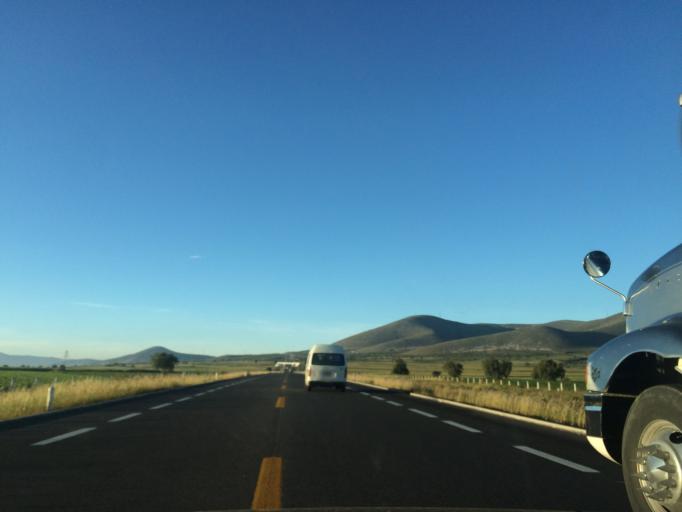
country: MX
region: Puebla
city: Morelos Canada
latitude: 18.7532
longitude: -97.4806
